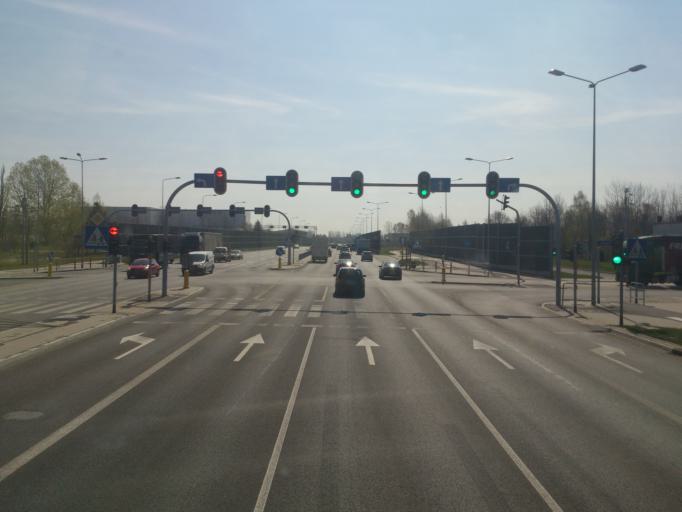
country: PL
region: Lodz Voivodeship
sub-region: Powiat lodzki wschodni
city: Starowa Gora
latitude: 51.7058
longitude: 19.4671
